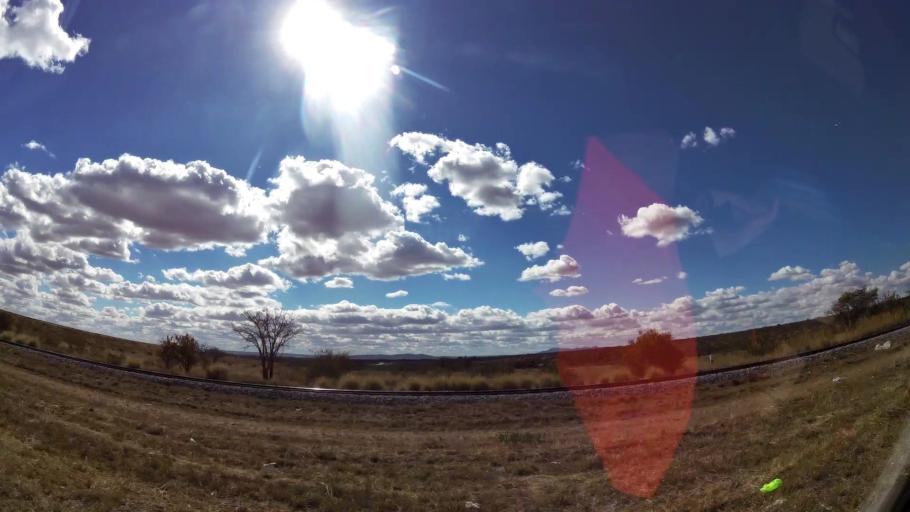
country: ZA
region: Limpopo
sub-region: Capricorn District Municipality
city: Polokwane
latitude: -23.8578
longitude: 29.5077
